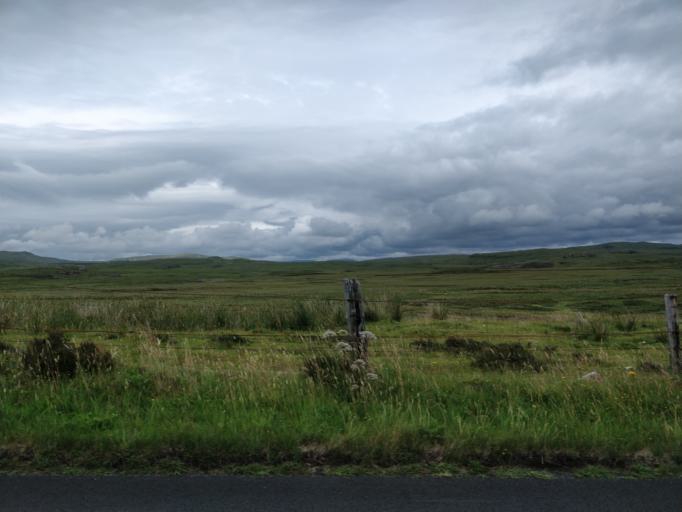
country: GB
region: Scotland
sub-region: Highland
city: Isle of Skye
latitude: 57.3710
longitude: -6.4570
